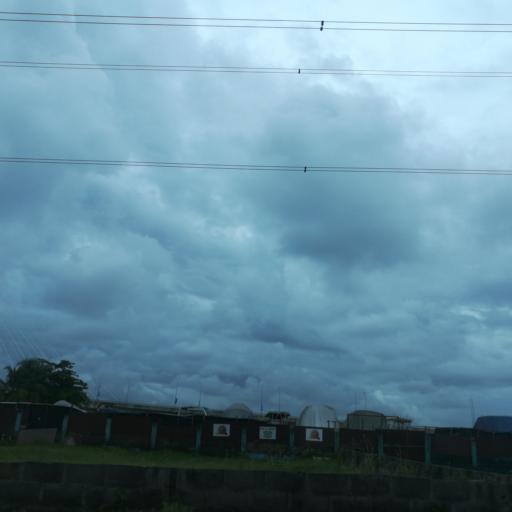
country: NG
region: Lagos
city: Ikoyi
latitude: 6.4483
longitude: 3.4549
